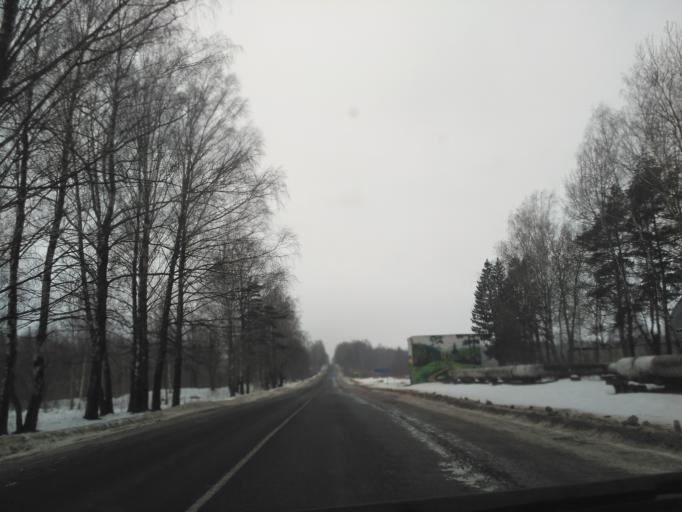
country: BY
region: Minsk
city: Horad Zhodzina
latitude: 54.0833
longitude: 28.3157
